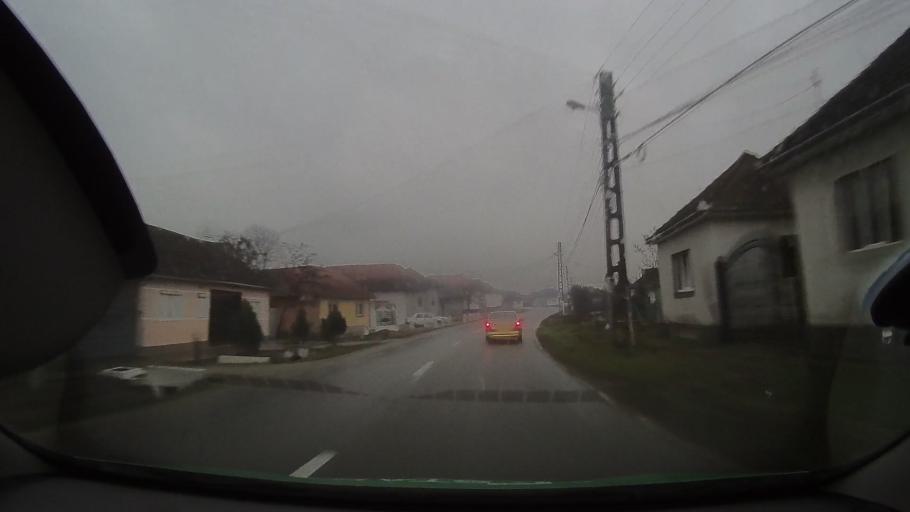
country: RO
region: Arad
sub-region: Comuna Craiova
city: Craiova
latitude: 46.5531
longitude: 21.9599
